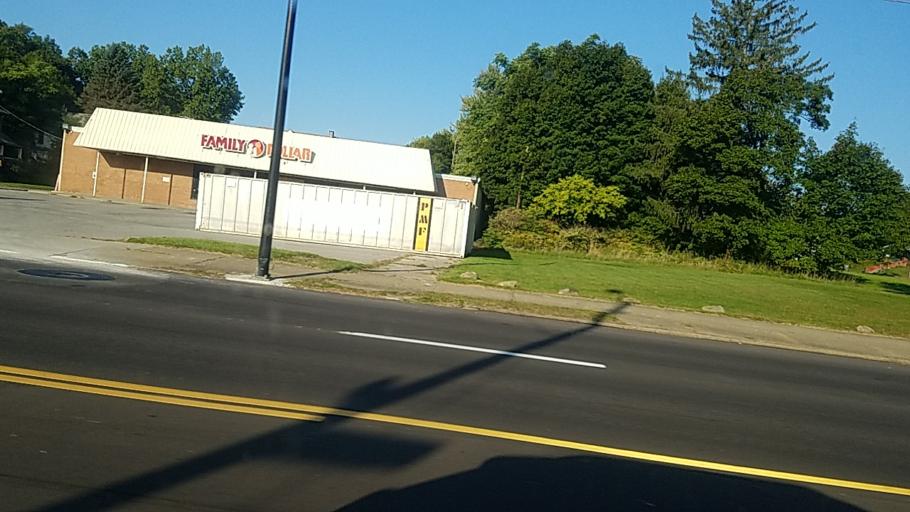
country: US
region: Ohio
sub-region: Mahoning County
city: Youngstown
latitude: 41.0774
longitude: -80.6569
